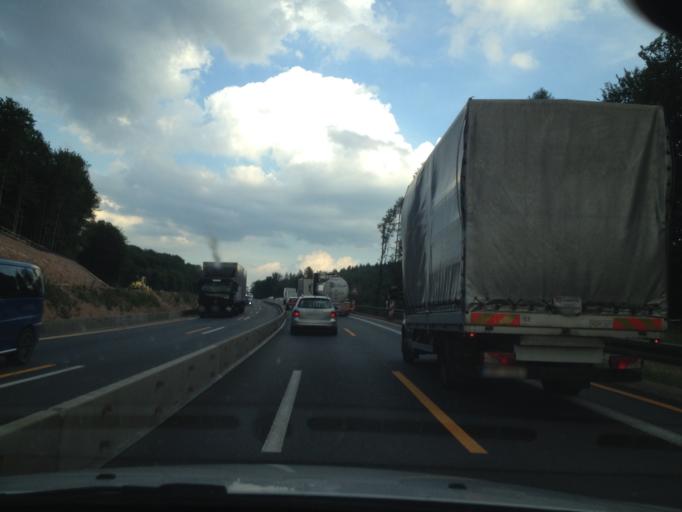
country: DE
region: Bavaria
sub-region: Regierungsbezirk Unterfranken
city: Weibersbrunn
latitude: 49.9476
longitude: 9.3336
